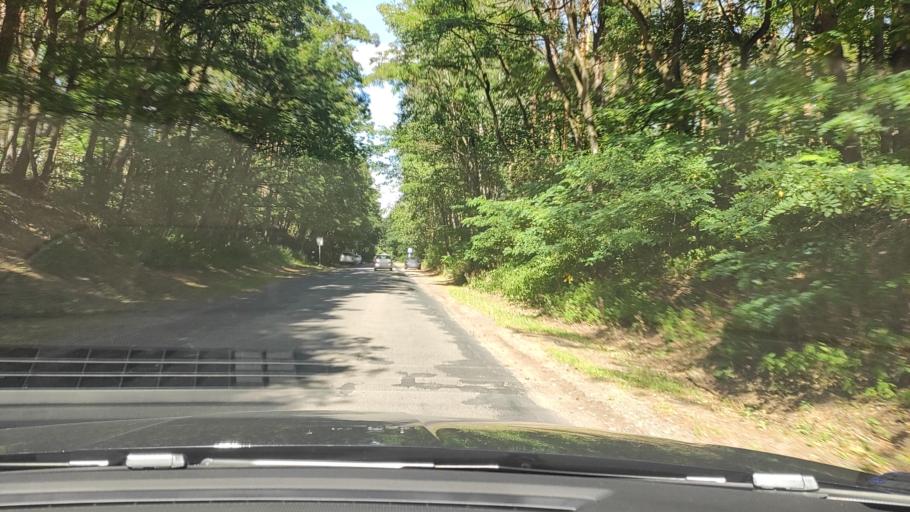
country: PL
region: Greater Poland Voivodeship
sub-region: Powiat poznanski
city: Kobylnica
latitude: 52.4527
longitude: 17.1614
